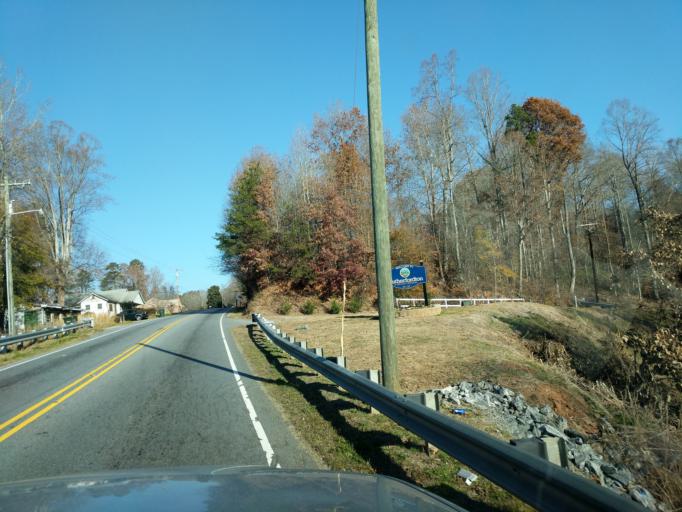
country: US
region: North Carolina
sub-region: Rutherford County
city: Rutherfordton
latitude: 35.3406
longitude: -81.9628
